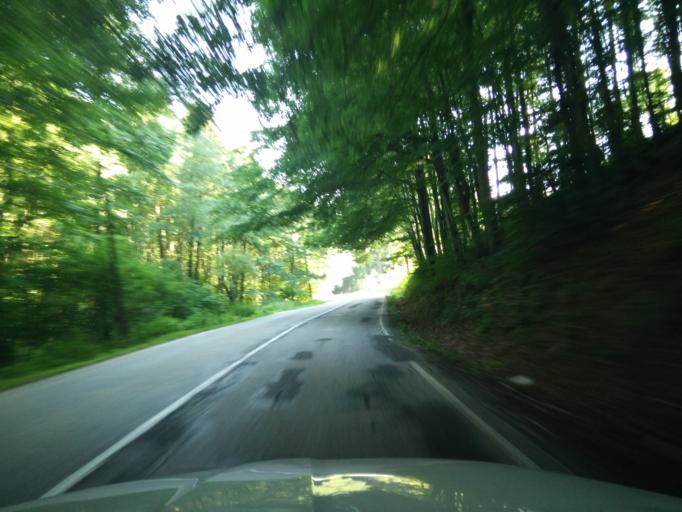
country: SK
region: Nitriansky
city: Bojnice
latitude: 48.8608
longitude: 18.4615
